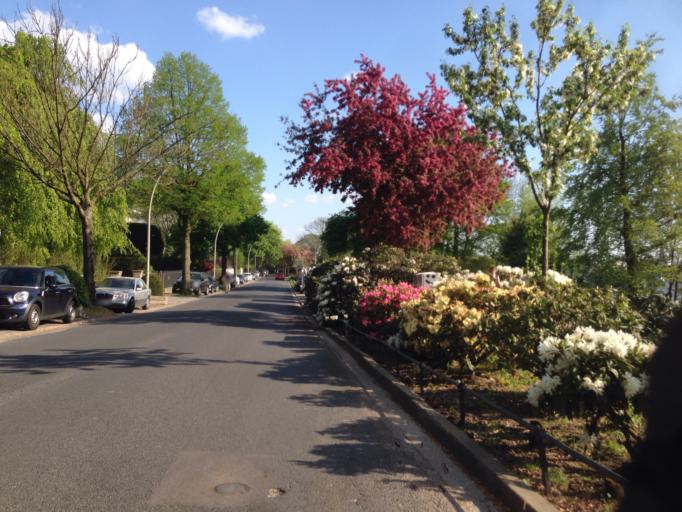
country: DE
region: Hamburg
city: Hamburg
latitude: 53.5715
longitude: 10.0092
